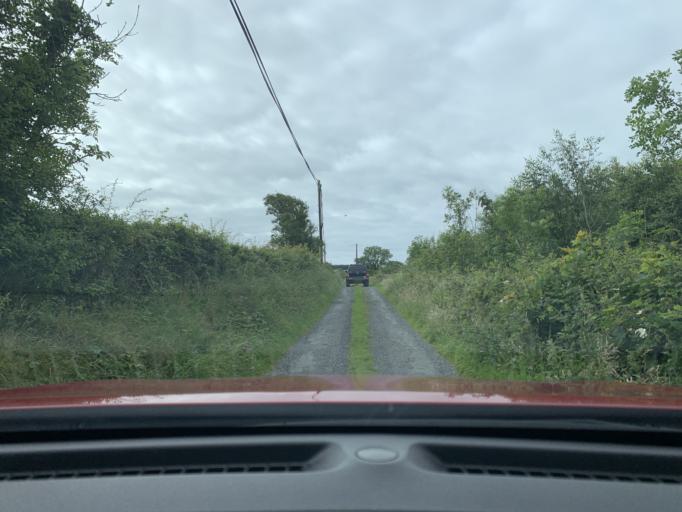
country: IE
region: Connaught
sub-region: Sligo
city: Sligo
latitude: 54.3786
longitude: -8.5209
